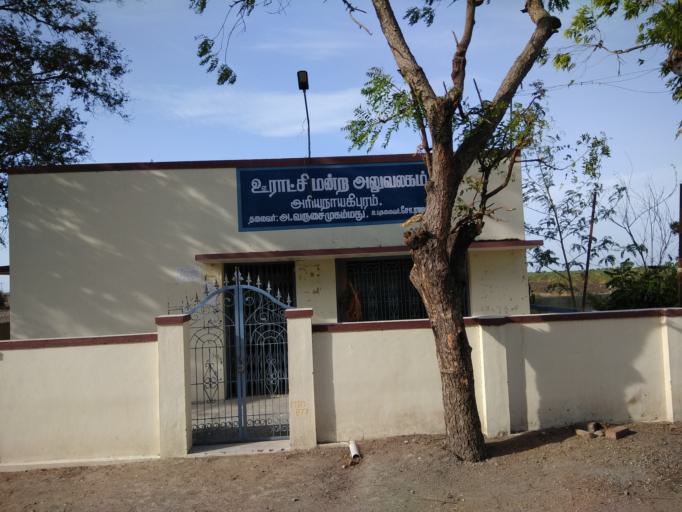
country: IN
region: Tamil Nadu
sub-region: Thoothukkudi
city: Vilattikulam
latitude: 9.1109
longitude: 78.2512
